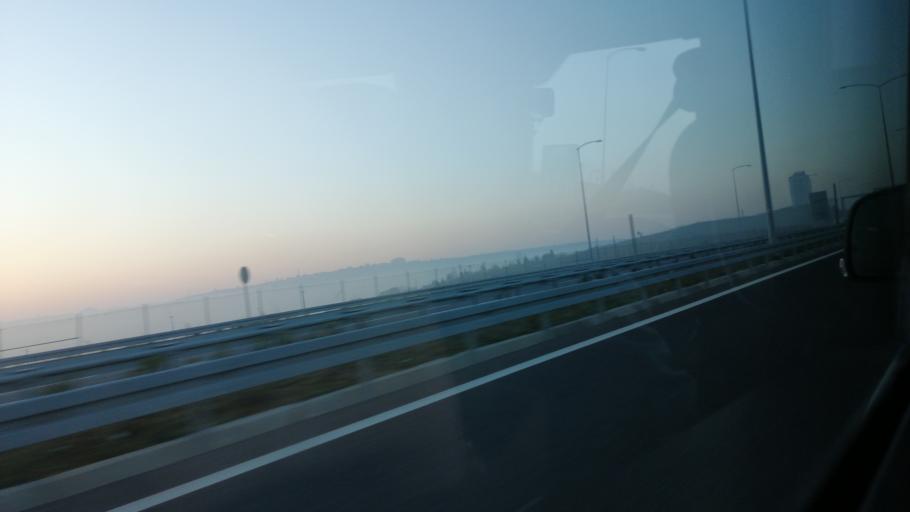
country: TR
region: Kocaeli
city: Tavsanli
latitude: 40.7819
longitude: 29.5170
